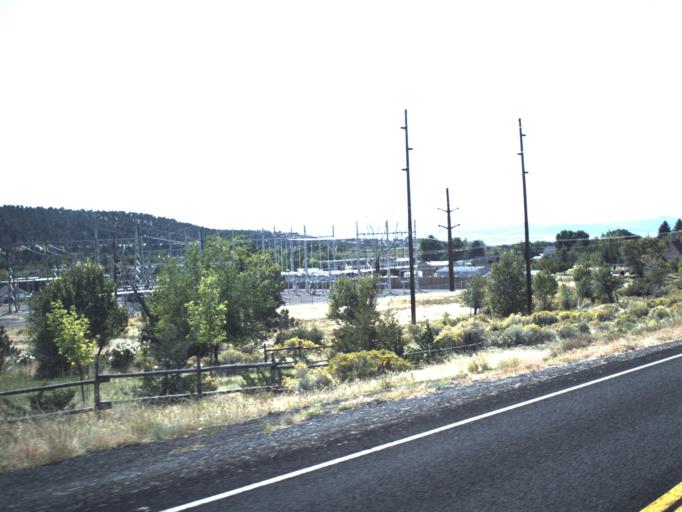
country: US
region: Utah
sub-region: Beaver County
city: Beaver
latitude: 38.2819
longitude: -112.5946
